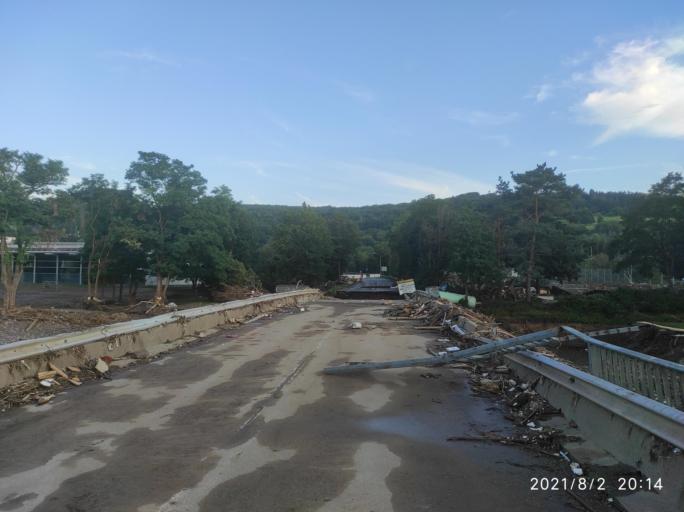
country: DE
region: Rheinland-Pfalz
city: Bad Neuenahr-Ahrweiler
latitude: 50.5426
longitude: 7.1213
